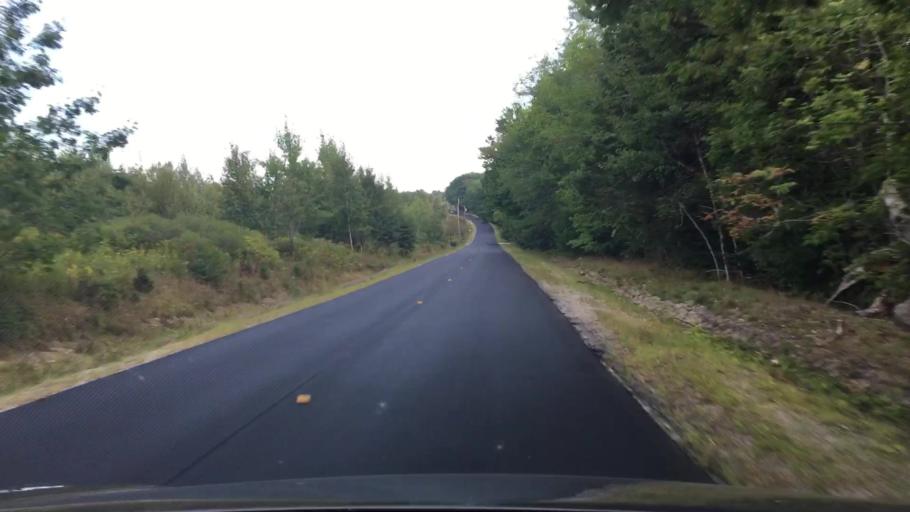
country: US
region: Maine
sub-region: Hancock County
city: Penobscot
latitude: 44.5412
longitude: -68.6164
